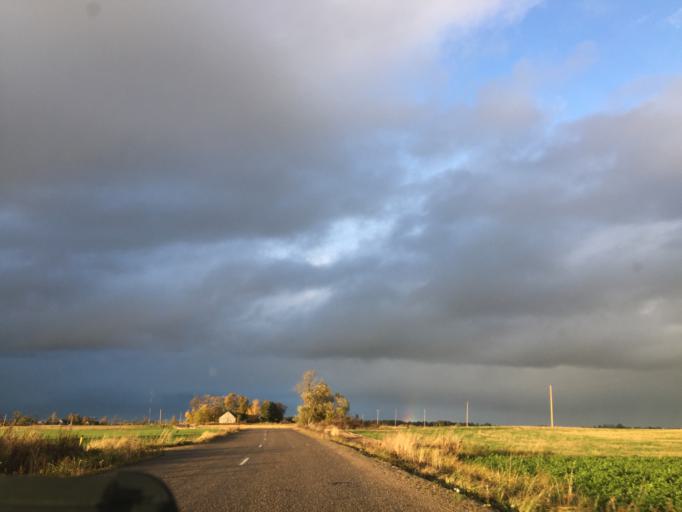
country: LV
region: Talsu Rajons
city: Sabile
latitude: 56.9312
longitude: 22.3970
